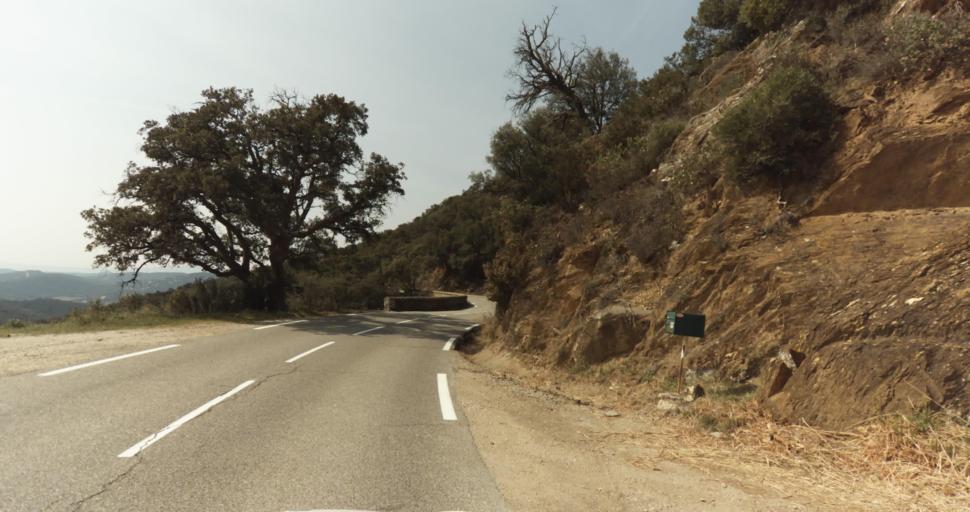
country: FR
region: Provence-Alpes-Cote d'Azur
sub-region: Departement du Var
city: Bormes-les-Mimosas
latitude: 43.1635
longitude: 6.3427
